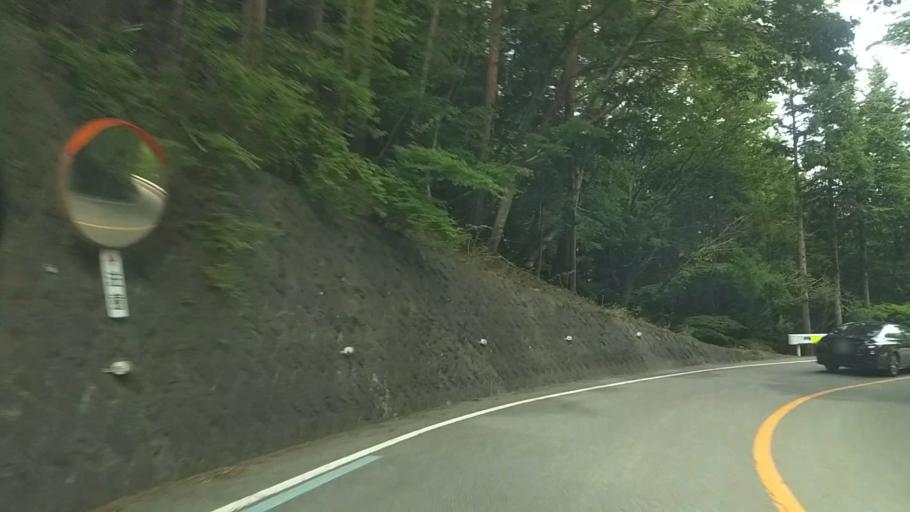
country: JP
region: Yamanashi
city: Fujikawaguchiko
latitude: 35.5079
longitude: 138.7098
